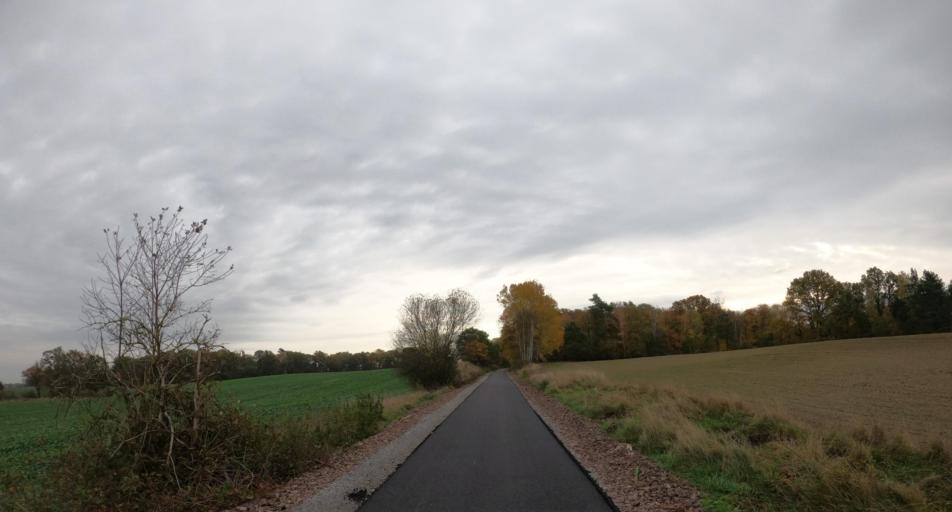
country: PL
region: West Pomeranian Voivodeship
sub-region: Powiat mysliborski
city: Nowogrodek Pomorski
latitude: 52.9869
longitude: 15.0838
